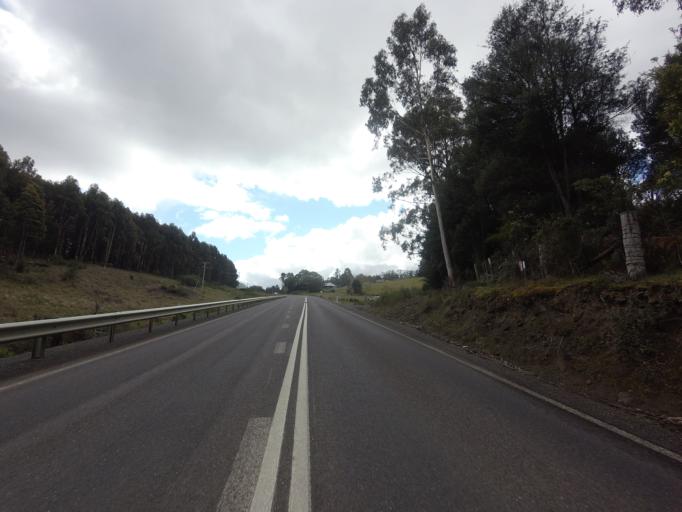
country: AU
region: Tasmania
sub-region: Huon Valley
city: Cygnet
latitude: -43.2592
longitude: 147.0062
